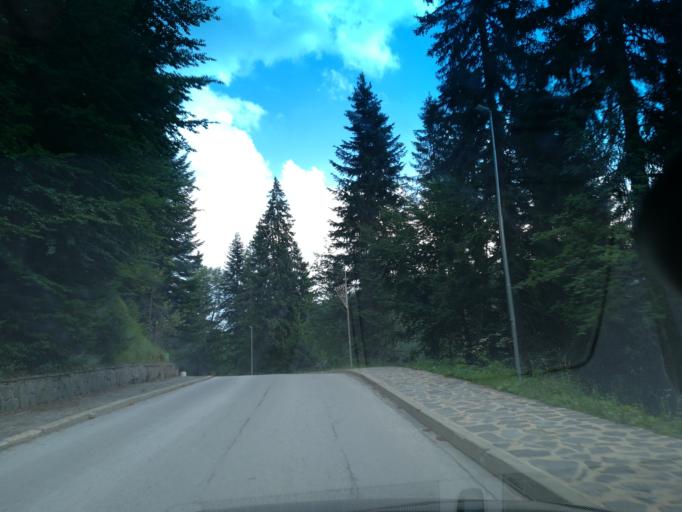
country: BG
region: Smolyan
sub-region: Obshtina Smolyan
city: Smolyan
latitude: 41.6545
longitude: 24.6917
